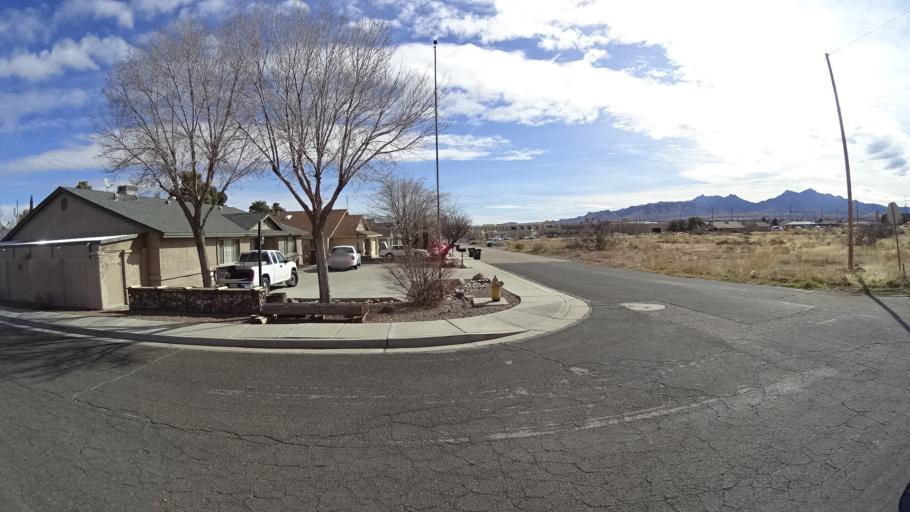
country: US
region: Arizona
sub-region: Mohave County
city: Kingman
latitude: 35.2208
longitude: -114.0425
